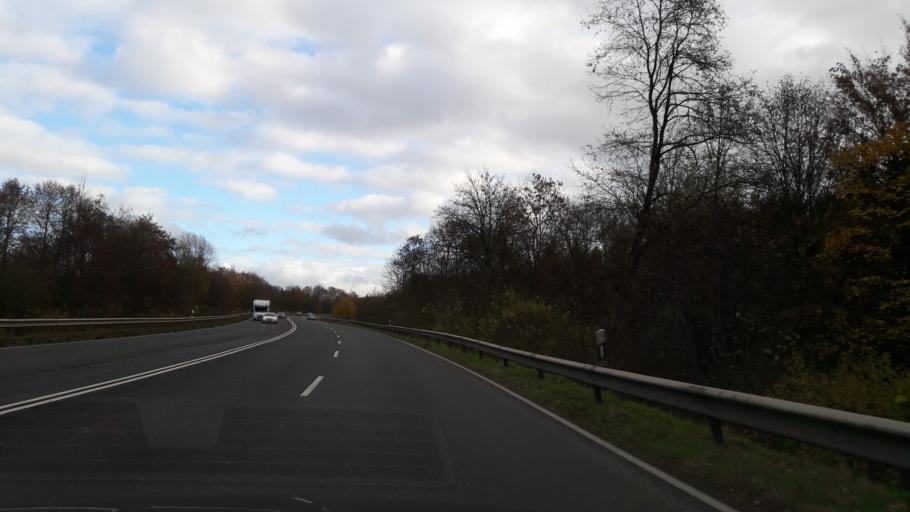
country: DE
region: Rheinland-Pfalz
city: Kenn
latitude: 49.7961
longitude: 6.7249
